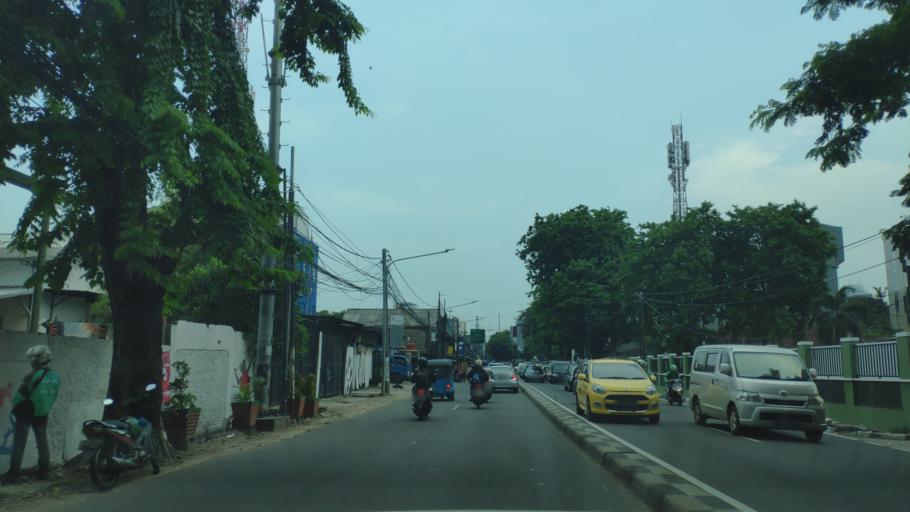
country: ID
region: Jakarta Raya
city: Jakarta
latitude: -6.1891
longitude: 106.8050
